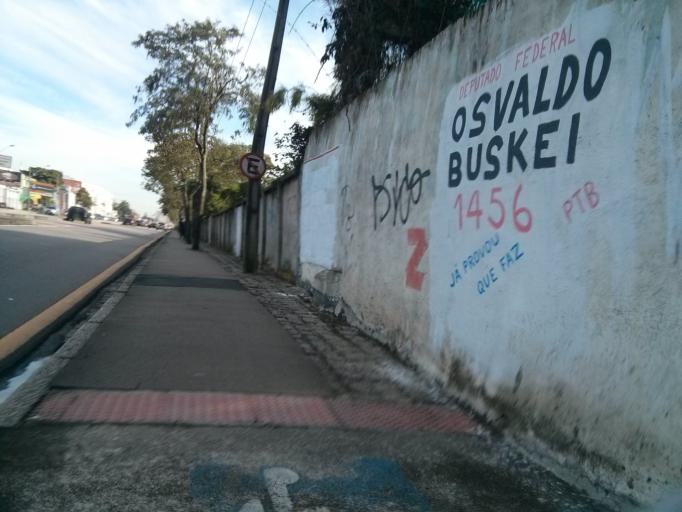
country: BR
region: Parana
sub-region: Curitiba
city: Curitiba
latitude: -25.4545
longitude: -49.2604
